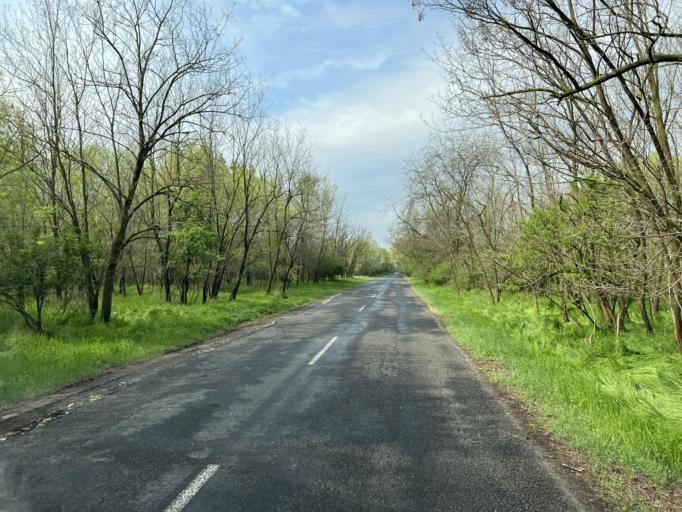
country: HU
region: Pest
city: Danszentmiklos
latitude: 47.1716
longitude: 19.5216
